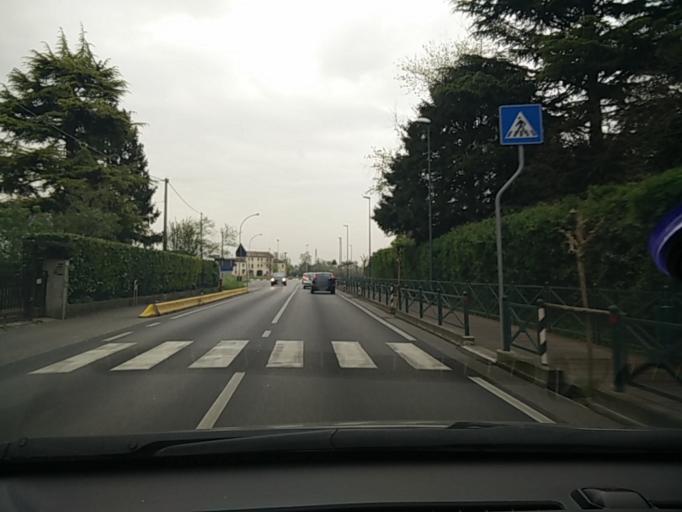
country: IT
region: Veneto
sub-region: Provincia di Treviso
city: Lancenigo-Villorba
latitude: 45.7150
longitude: 12.2750
